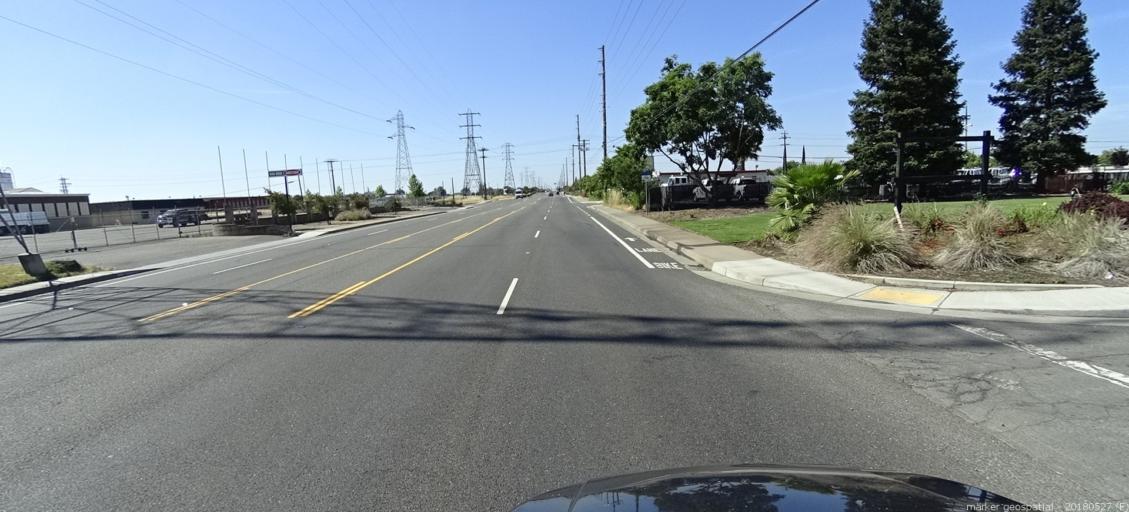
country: US
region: California
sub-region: Sacramento County
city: Florin
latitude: 38.5334
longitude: -121.4093
